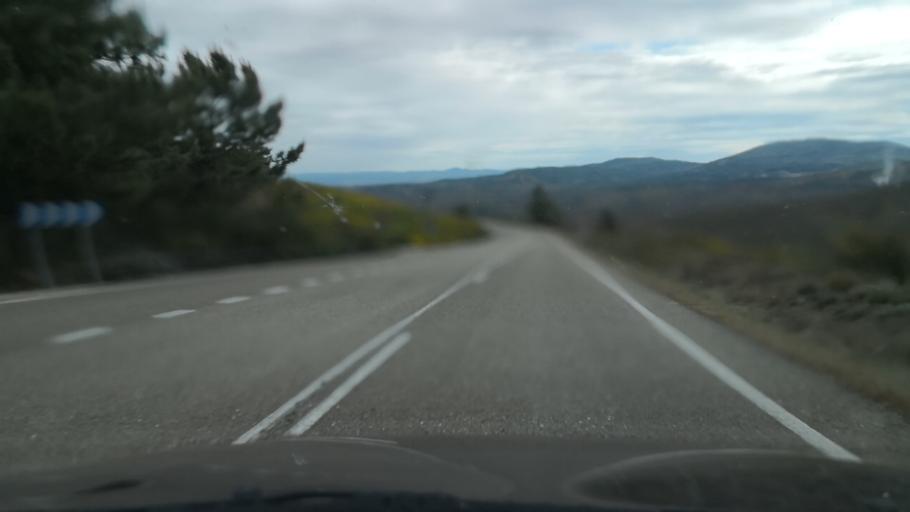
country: ES
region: Extremadura
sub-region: Provincia de Caceres
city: Acebo
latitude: 40.2138
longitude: -6.6755
